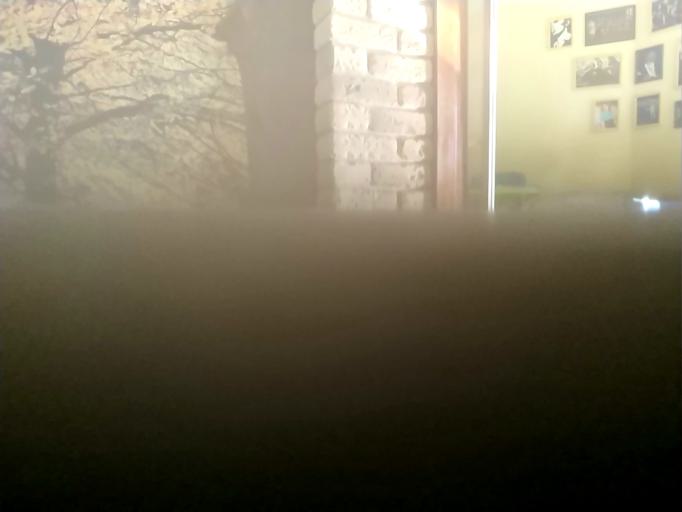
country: RU
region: Smolensk
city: Temkino
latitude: 54.8976
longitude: 34.9766
